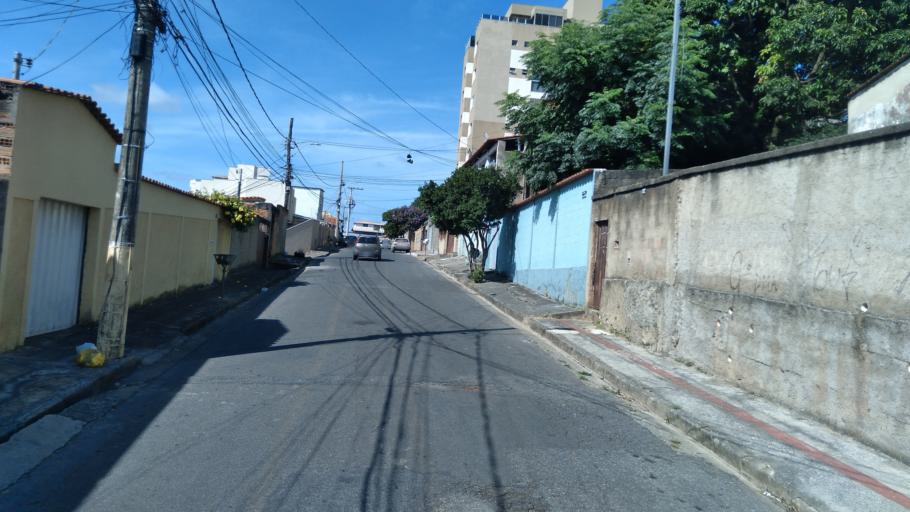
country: BR
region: Minas Gerais
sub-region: Belo Horizonte
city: Belo Horizonte
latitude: -19.8790
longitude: -43.9197
